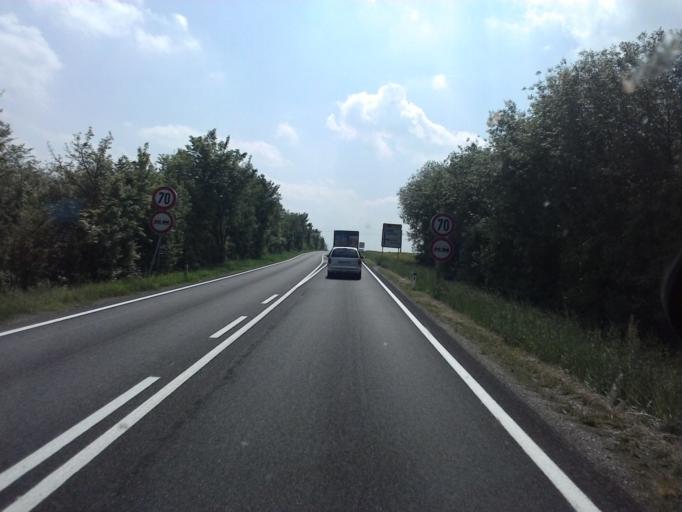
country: AT
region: Upper Austria
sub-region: Politischer Bezirk Steyr-Land
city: Sierning
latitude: 48.0482
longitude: 14.3248
